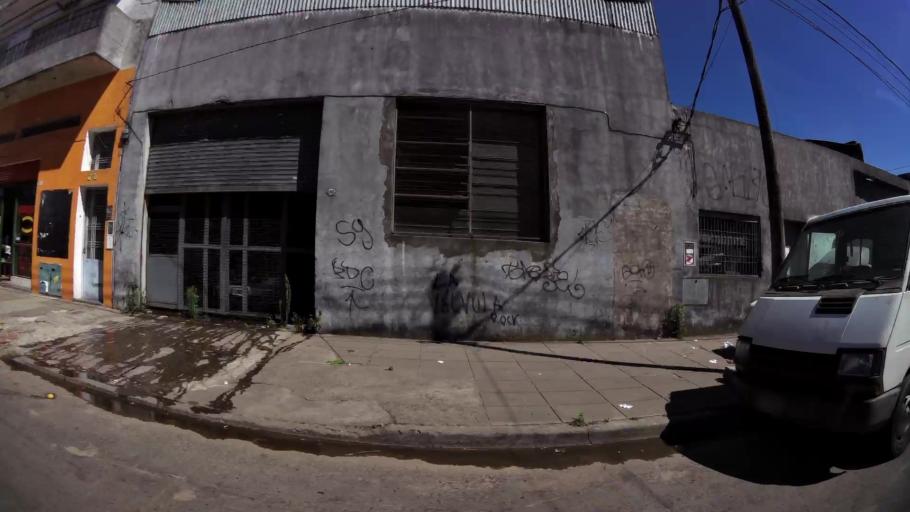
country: AR
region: Buenos Aires
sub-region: Partido de General San Martin
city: General San Martin
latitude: -34.5609
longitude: -58.5274
